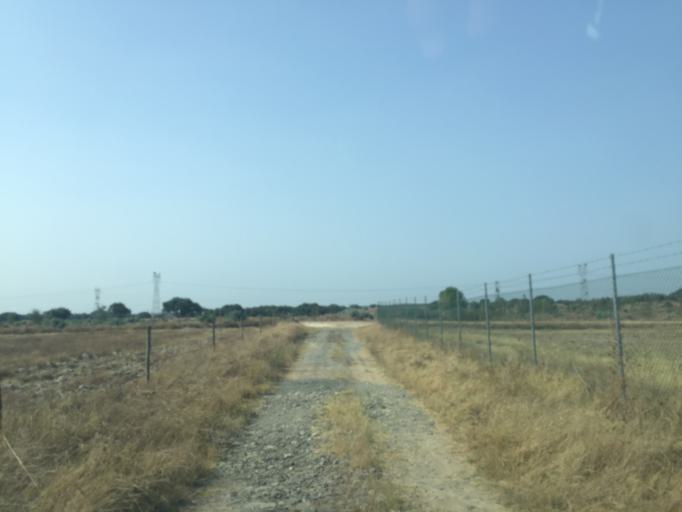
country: PT
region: Beja
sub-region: Aljustrel
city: Aljustrel
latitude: 38.0241
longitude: -8.3587
